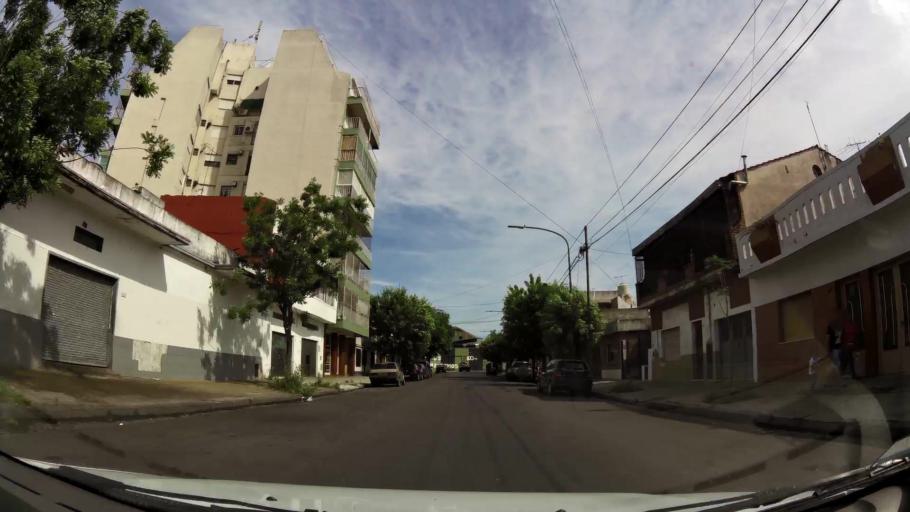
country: AR
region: Buenos Aires F.D.
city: Villa Lugano
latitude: -34.6715
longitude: -58.4992
